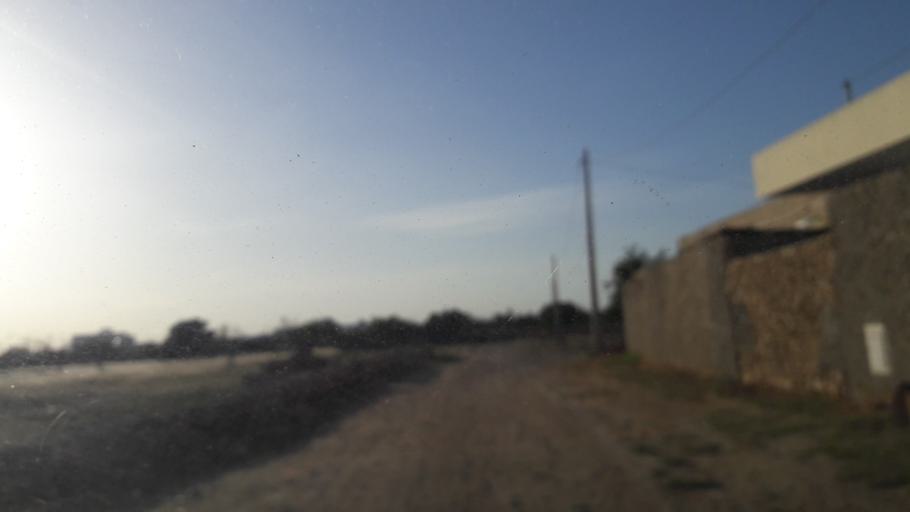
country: TN
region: Safaqis
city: Sfax
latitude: 34.8198
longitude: 10.7377
